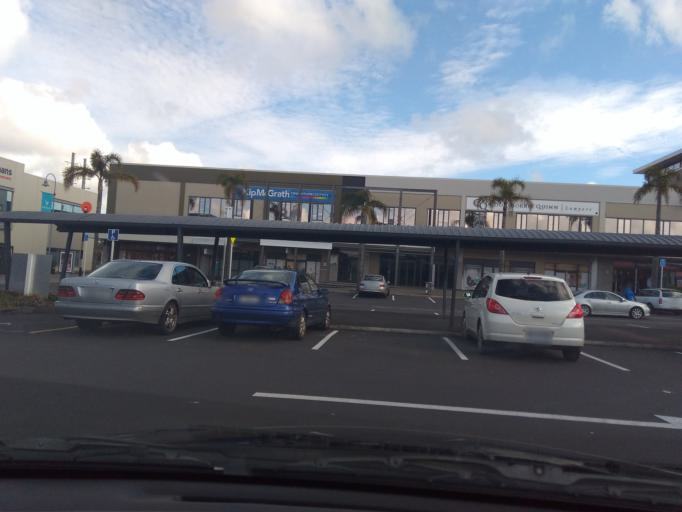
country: NZ
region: Auckland
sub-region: Auckland
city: Rosebank
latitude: -36.8211
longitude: 174.6137
